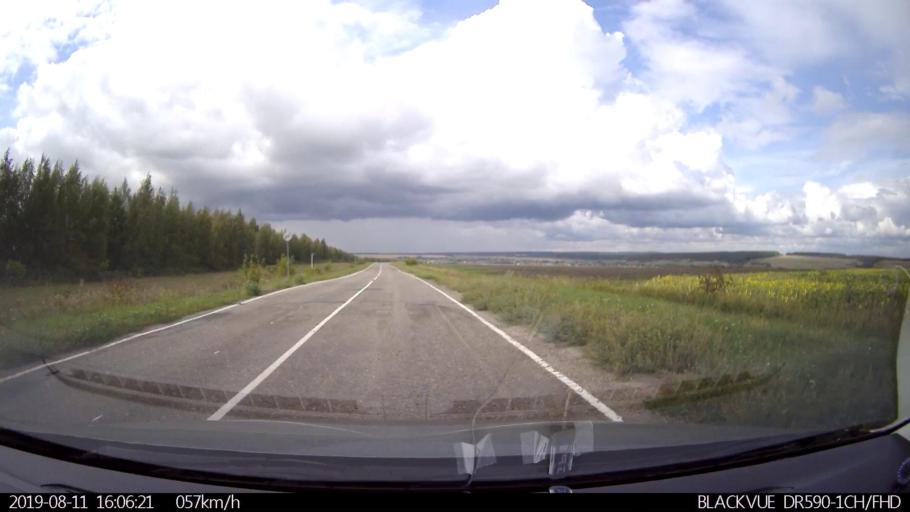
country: RU
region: Ulyanovsk
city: Ignatovka
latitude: 53.9681
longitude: 47.6489
